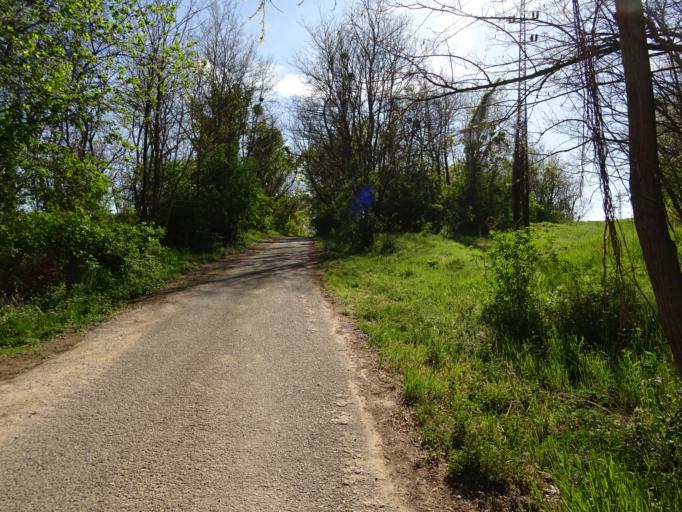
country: HU
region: Gyor-Moson-Sopron
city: Bakonyszentlaszlo
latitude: 47.3804
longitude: 17.7983
